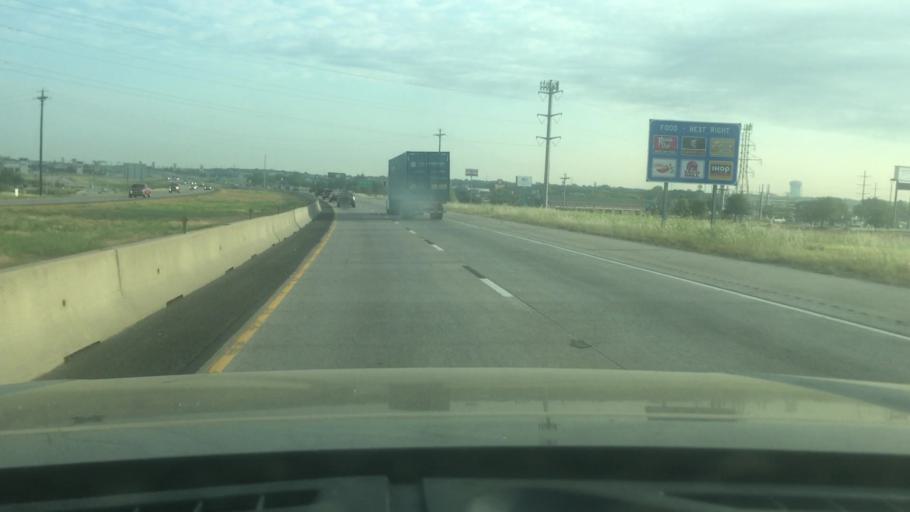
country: US
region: Texas
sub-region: Tarrant County
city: Euless
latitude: 32.8630
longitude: -97.1028
